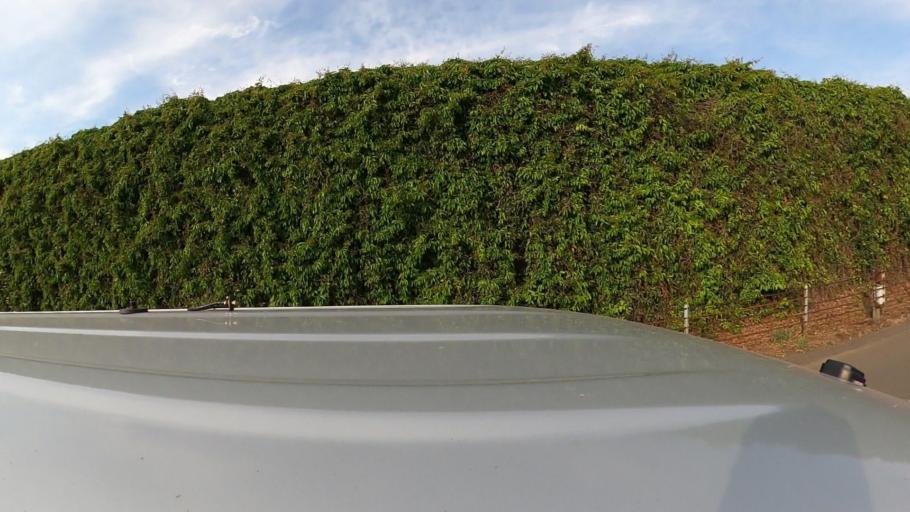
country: JP
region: Saitama
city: Oi
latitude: 35.8209
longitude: 139.5205
